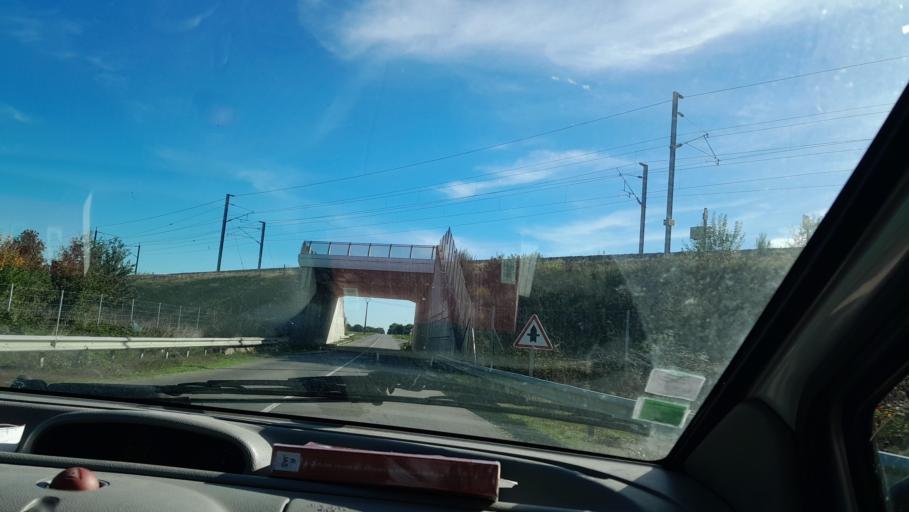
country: FR
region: Brittany
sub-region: Departement d'Ille-et-Vilaine
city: Argentre-du-Plessis
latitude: 48.0327
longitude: -1.1418
